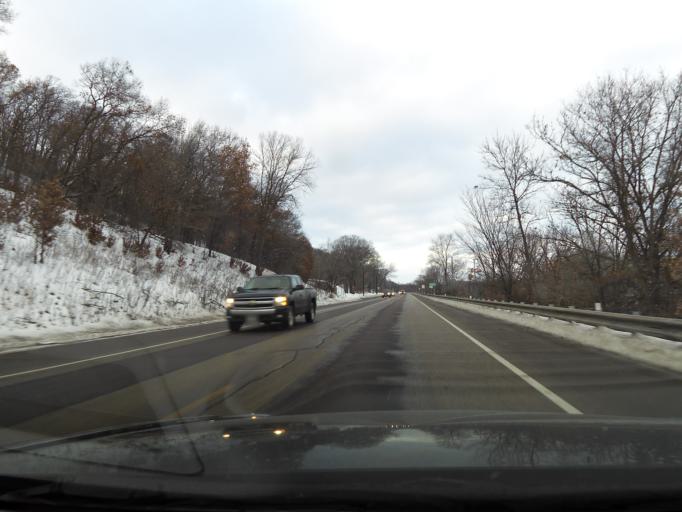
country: US
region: Wisconsin
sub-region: Saint Croix County
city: North Hudson
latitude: 44.9988
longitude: -92.7784
